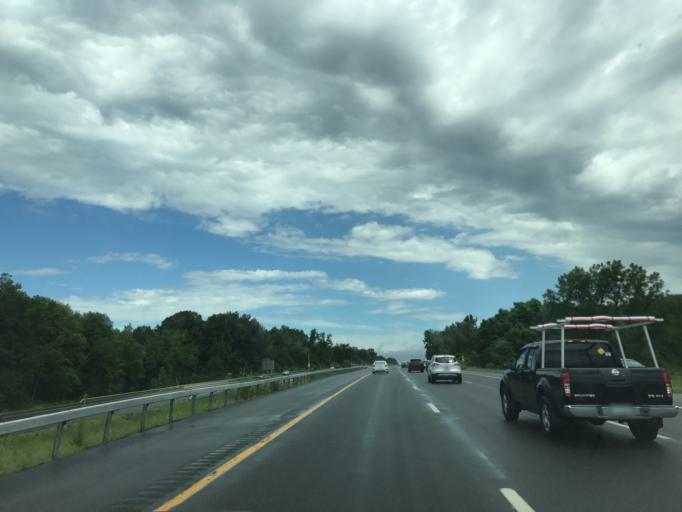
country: US
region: New York
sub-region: Albany County
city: Cohoes
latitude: 42.7743
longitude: -73.7605
